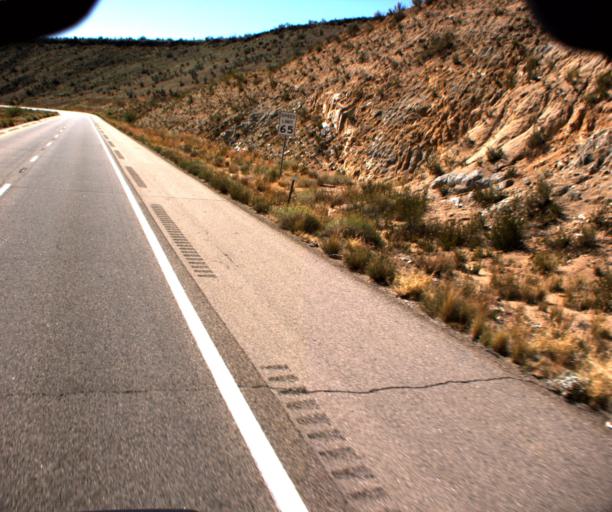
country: US
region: Arizona
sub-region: Yavapai County
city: Bagdad
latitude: 34.4503
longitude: -113.2863
